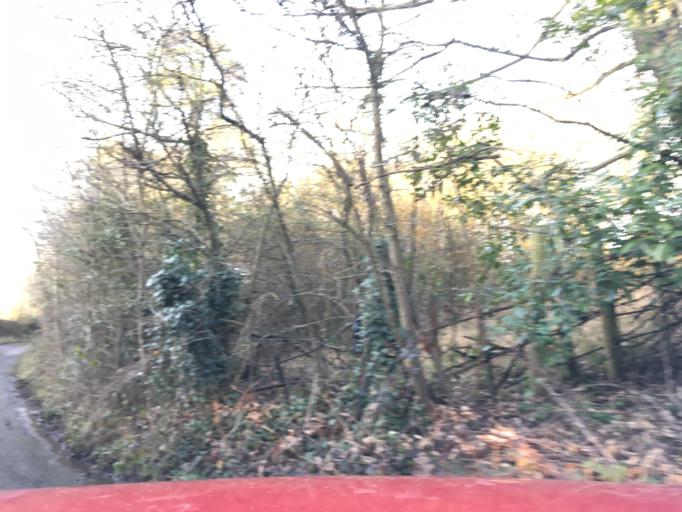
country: GB
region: England
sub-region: Warwickshire
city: Stratford-upon-Avon
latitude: 52.2094
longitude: -1.6956
